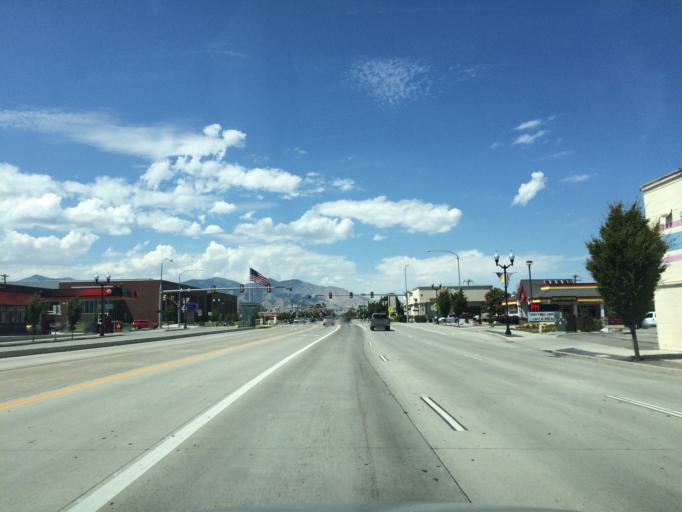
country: US
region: Utah
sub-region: Salt Lake County
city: West Valley City
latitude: 40.6967
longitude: -111.9755
